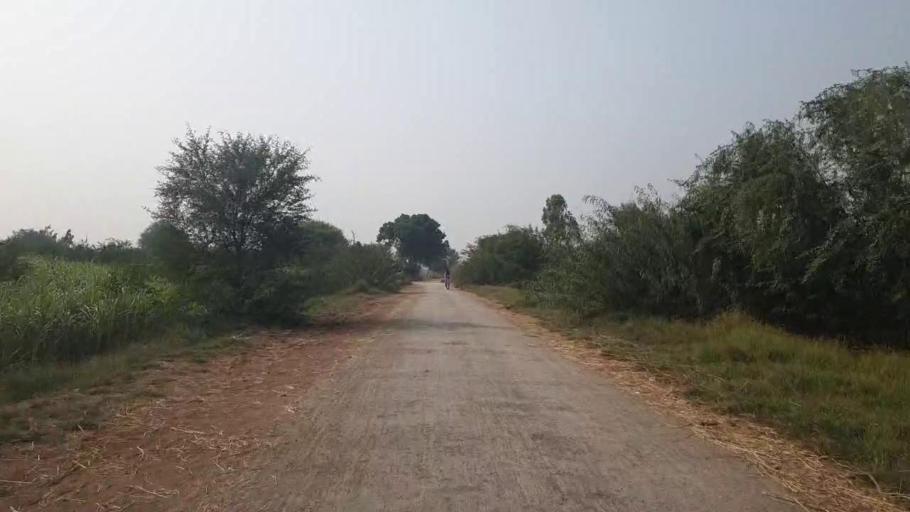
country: PK
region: Sindh
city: Tando Jam
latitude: 25.2782
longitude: 68.4925
